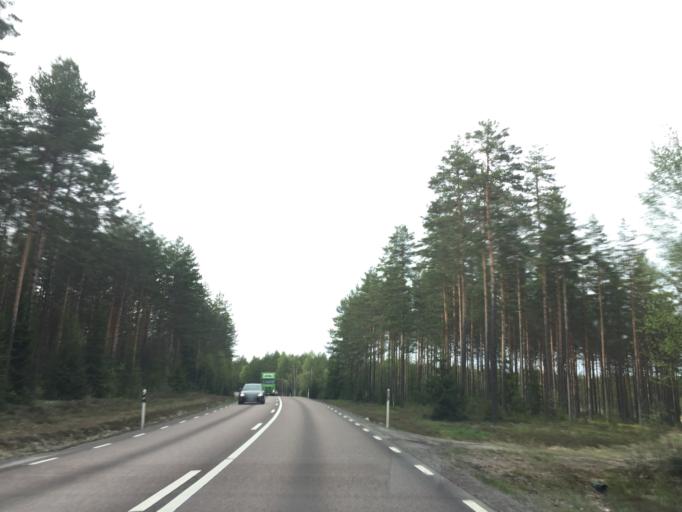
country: SE
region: Vaermland
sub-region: Eda Kommun
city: Charlottenberg
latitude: 59.9003
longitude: 12.2794
